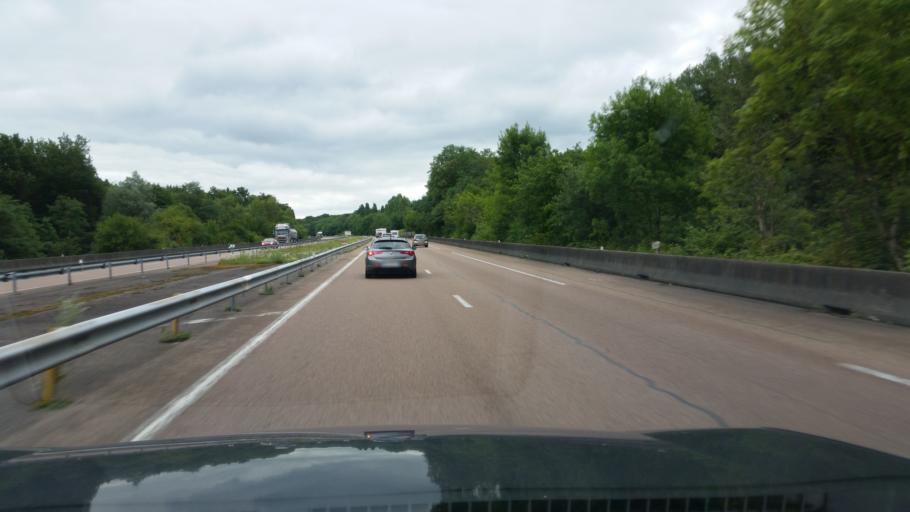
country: FR
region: Franche-Comte
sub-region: Departement du Jura
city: Bletterans
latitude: 46.6974
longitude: 5.4696
